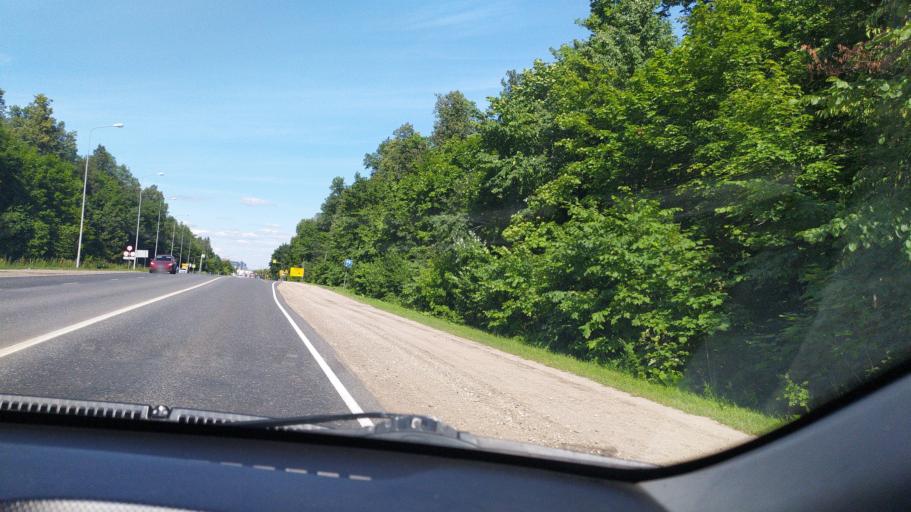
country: RU
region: Chuvashia
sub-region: Cheboksarskiy Rayon
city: Cheboksary
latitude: 56.0947
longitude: 47.2551
